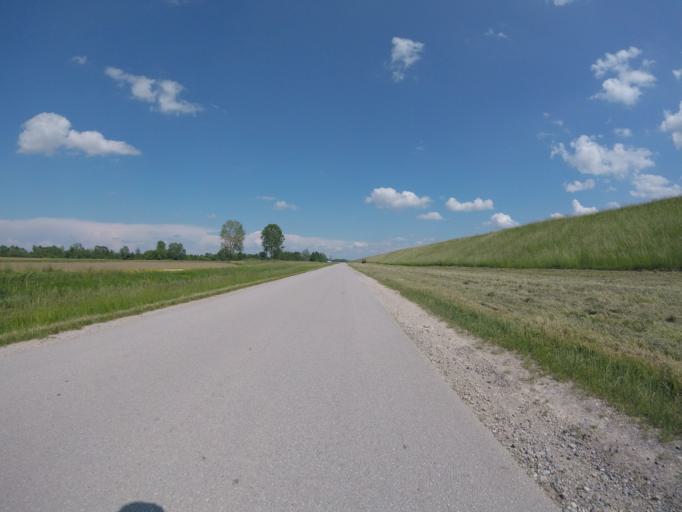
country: HR
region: Zagrebacka
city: Kuce
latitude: 45.6691
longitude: 16.1807
